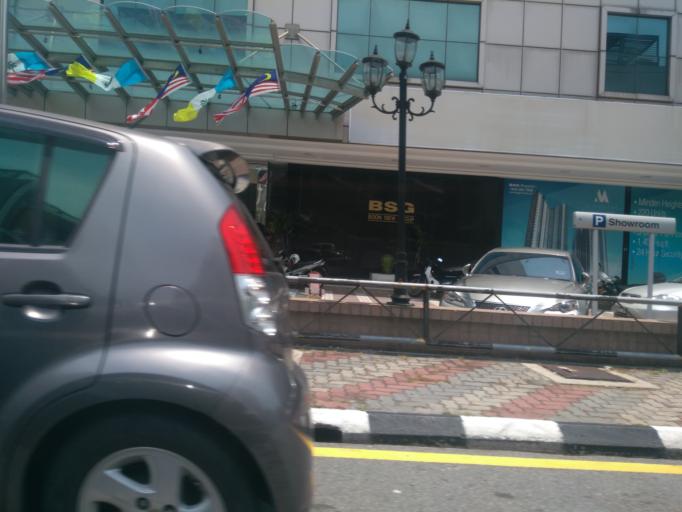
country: MY
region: Penang
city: George Town
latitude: 5.4223
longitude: 100.3363
